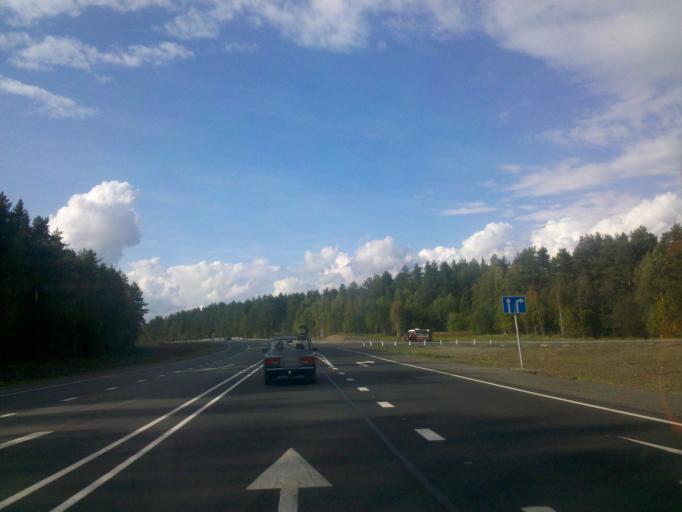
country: RU
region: Republic of Karelia
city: Shuya
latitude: 61.8552
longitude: 34.1797
